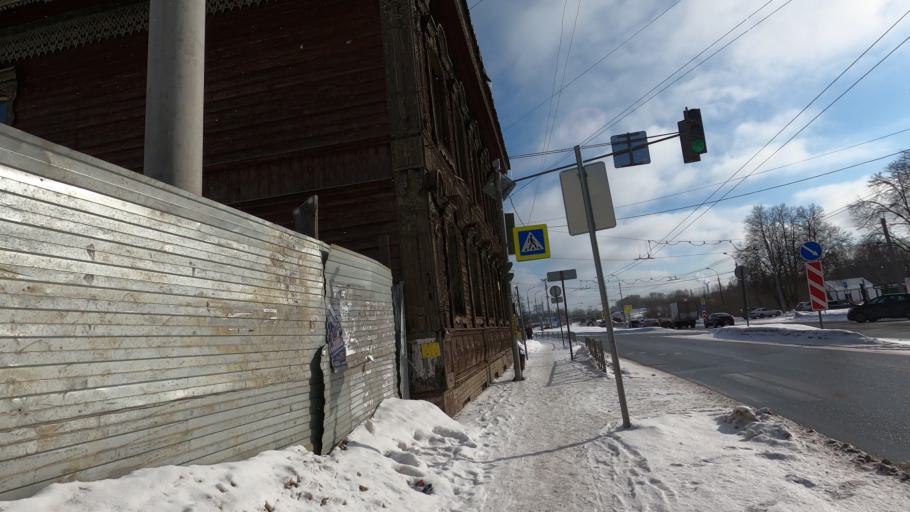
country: RU
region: Jaroslavl
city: Rybinsk
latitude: 58.0464
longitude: 38.8509
